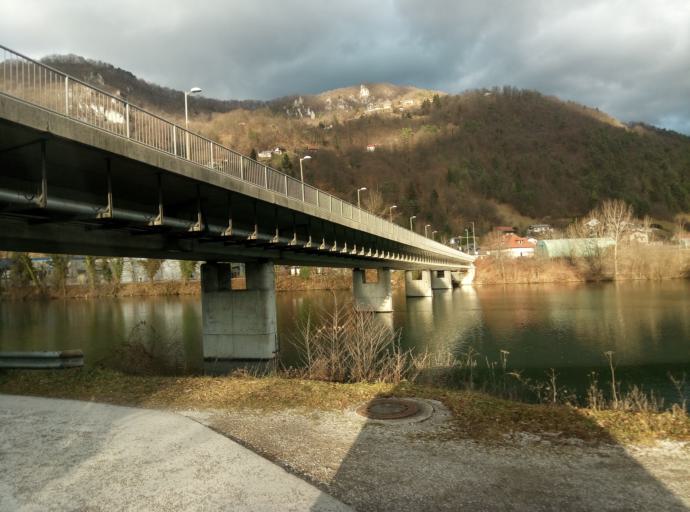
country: SI
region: Radece
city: Radece
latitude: 46.0629
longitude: 15.1890
